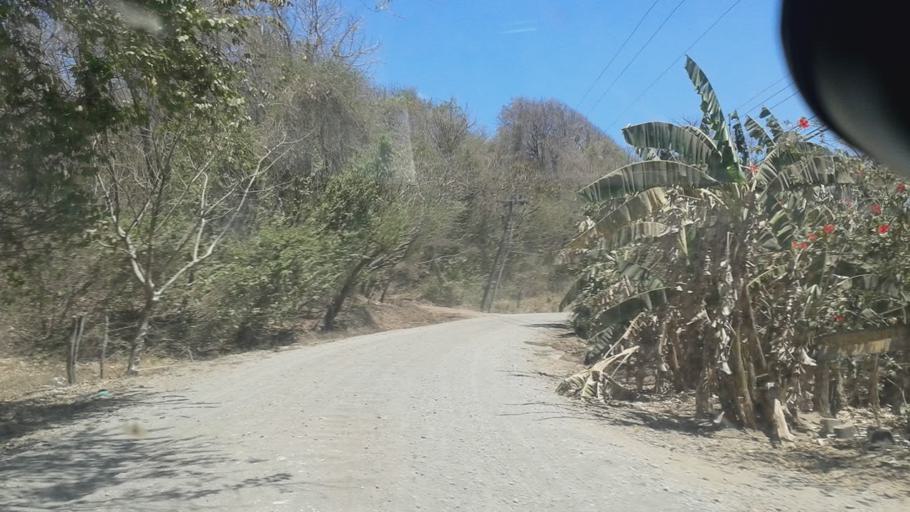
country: CR
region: Guanacaste
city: Samara
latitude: 10.0049
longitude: -85.7096
